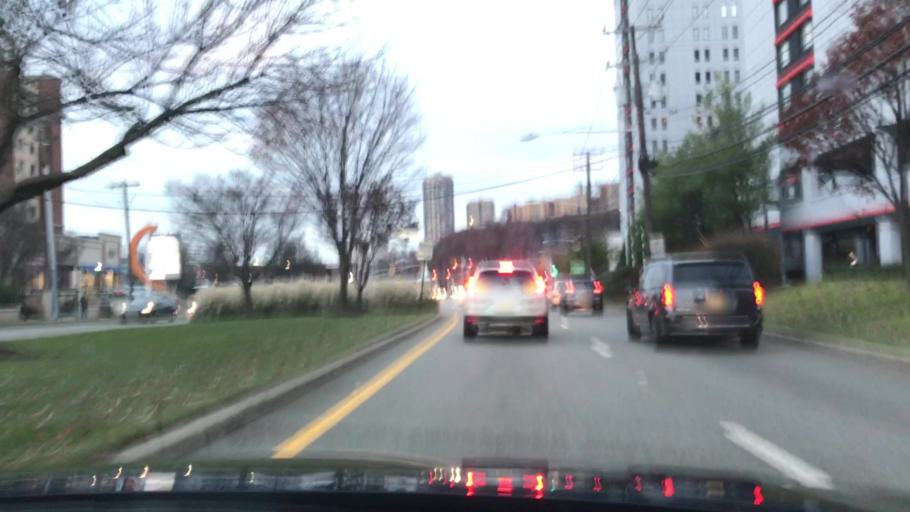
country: US
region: New Jersey
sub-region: Bergen County
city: Fairview
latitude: 40.8080
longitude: -73.9902
